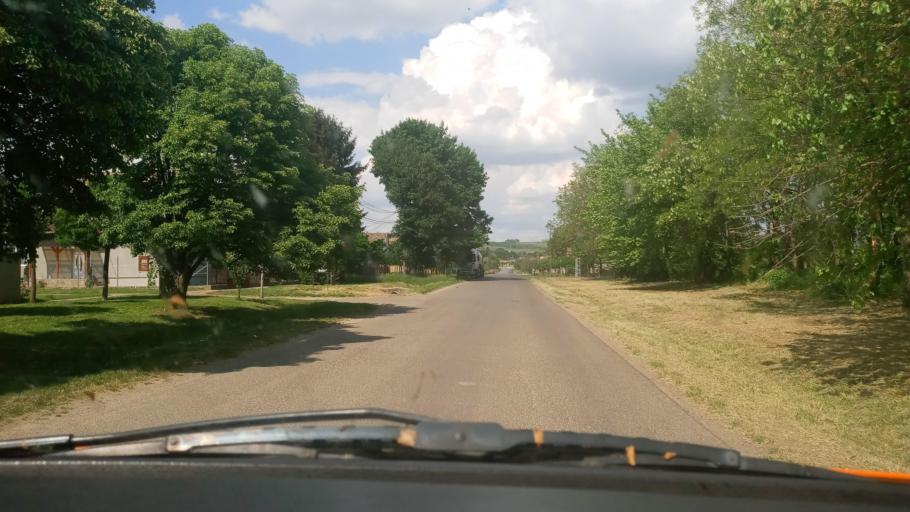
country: HU
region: Baranya
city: Siklos
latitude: 45.8545
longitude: 18.3609
